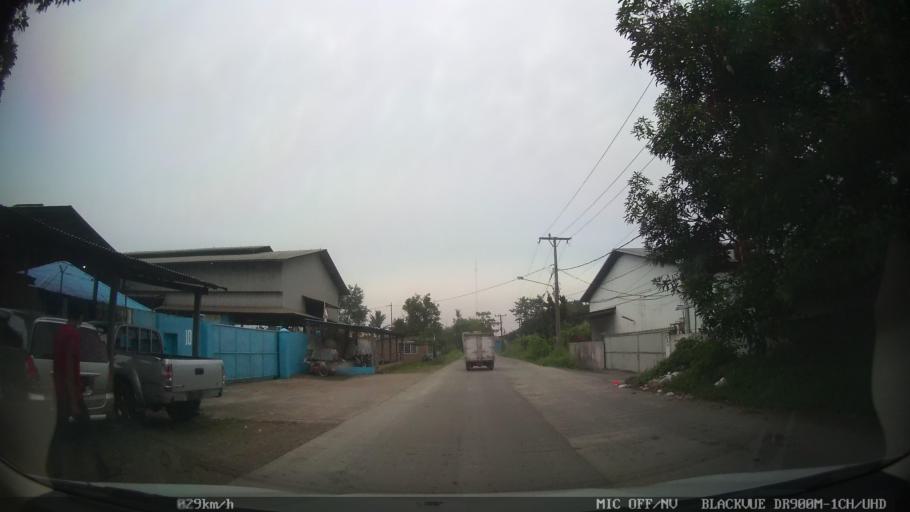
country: ID
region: North Sumatra
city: Deli Tua
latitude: 3.5369
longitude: 98.7262
